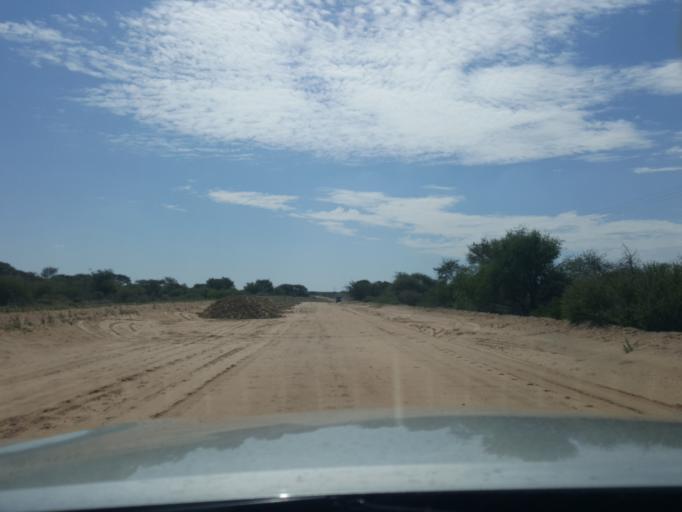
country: BW
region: Kweneng
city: Letlhakeng
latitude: -24.0470
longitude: 25.0194
